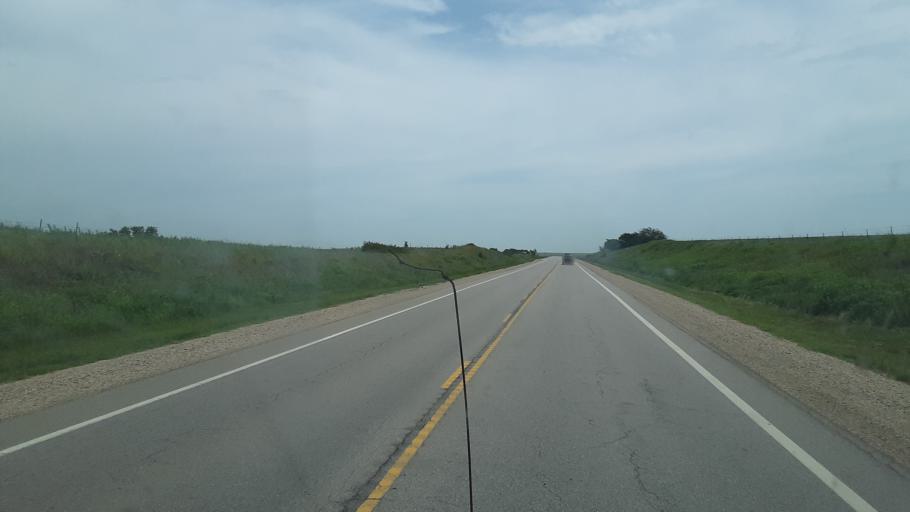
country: US
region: Kansas
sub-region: Greenwood County
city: Eureka
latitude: 37.8138
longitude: -96.4859
